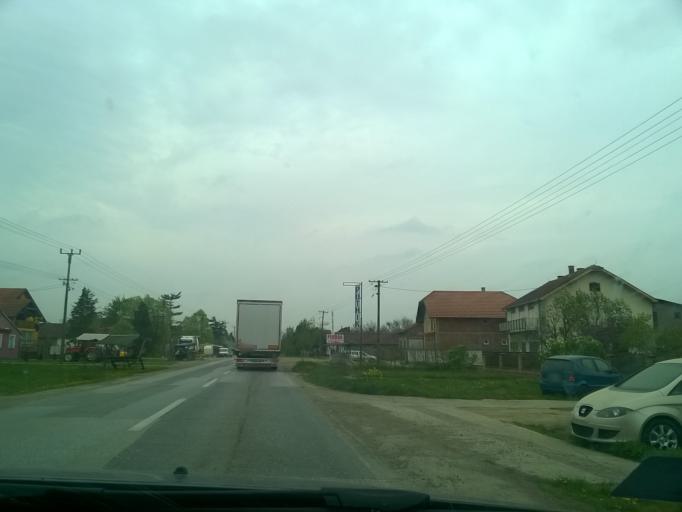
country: RS
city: Hrtkovci
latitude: 44.8886
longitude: 19.7637
